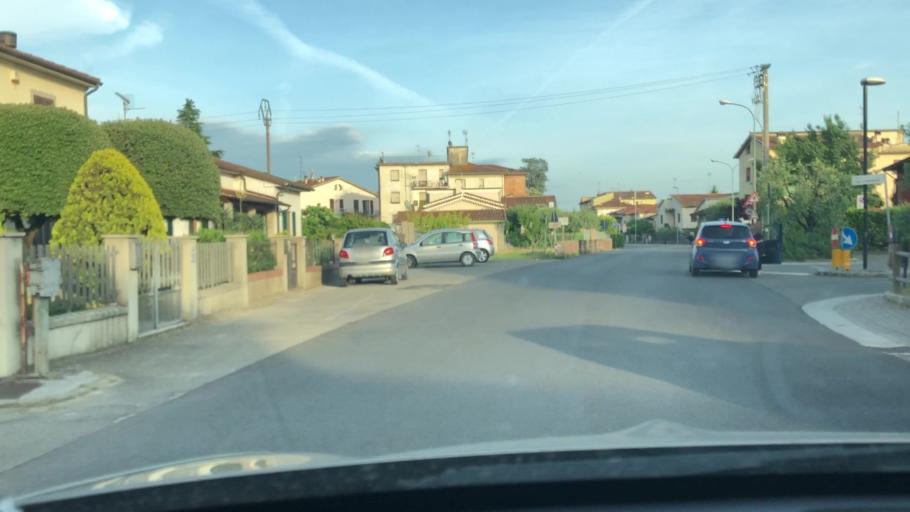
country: IT
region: Tuscany
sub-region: Province of Pisa
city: Forcoli
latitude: 43.6037
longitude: 10.7067
